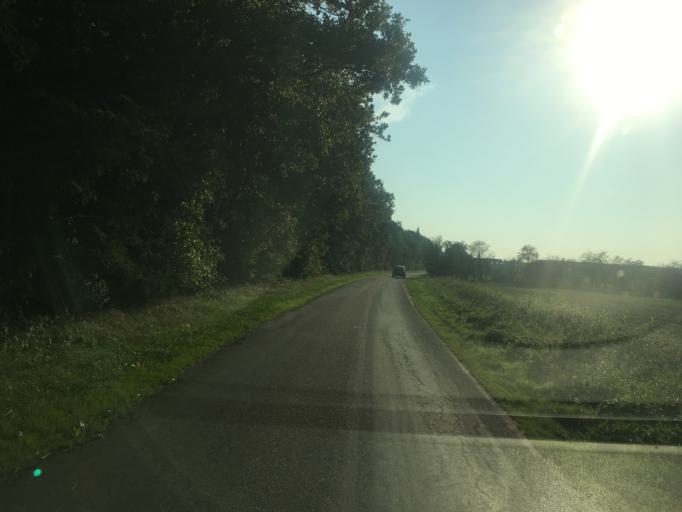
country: DE
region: Schleswig-Holstein
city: Bramstedtlund
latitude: 54.9251
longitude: 9.0569
